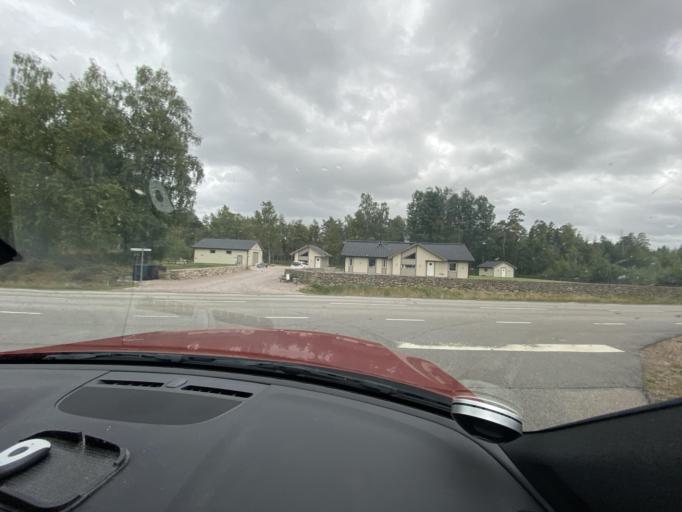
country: SE
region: Kronoberg
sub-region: Markaryds Kommun
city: Markaryd
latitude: 56.4601
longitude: 13.6199
